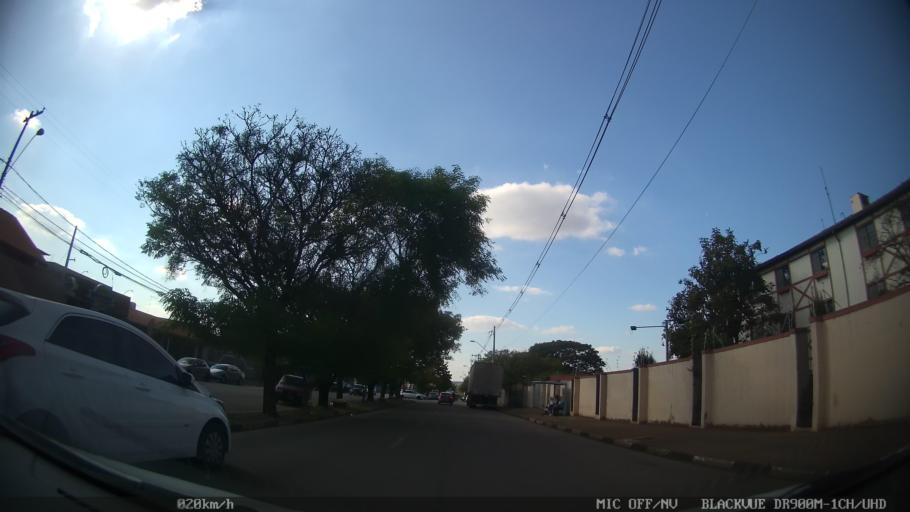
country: BR
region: Sao Paulo
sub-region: Sumare
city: Sumare
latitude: -22.8159
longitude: -47.2863
